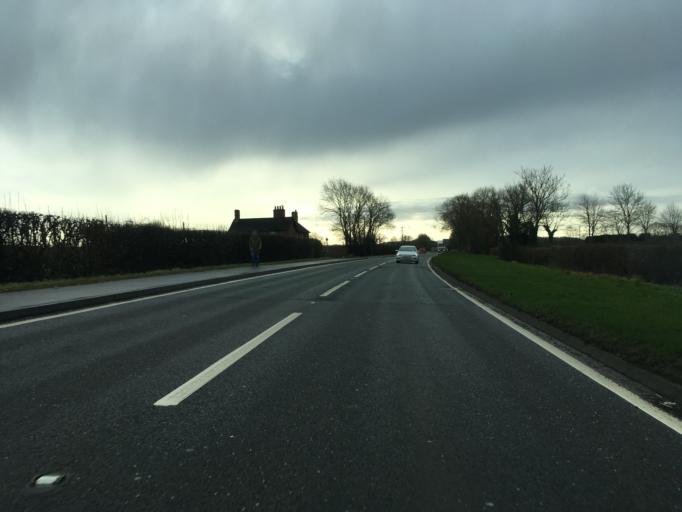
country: GB
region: England
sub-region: Worcestershire
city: Evesham
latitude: 52.0677
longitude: -1.9546
